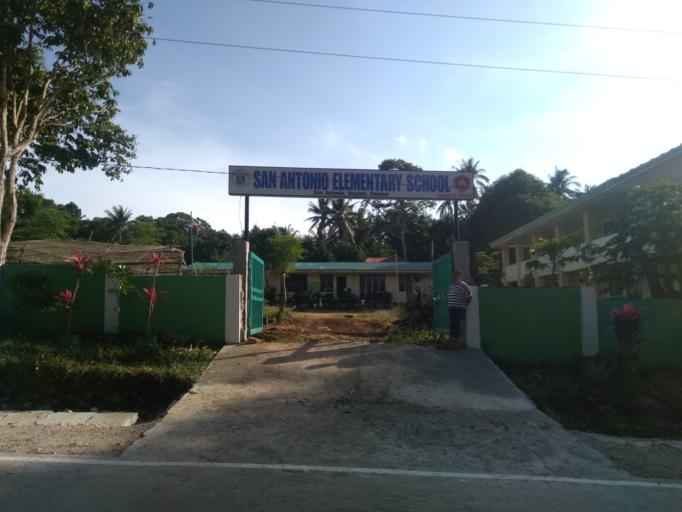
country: PH
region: Central Visayas
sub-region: Province of Siquijor
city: Siquijor
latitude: 9.1817
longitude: 123.5406
